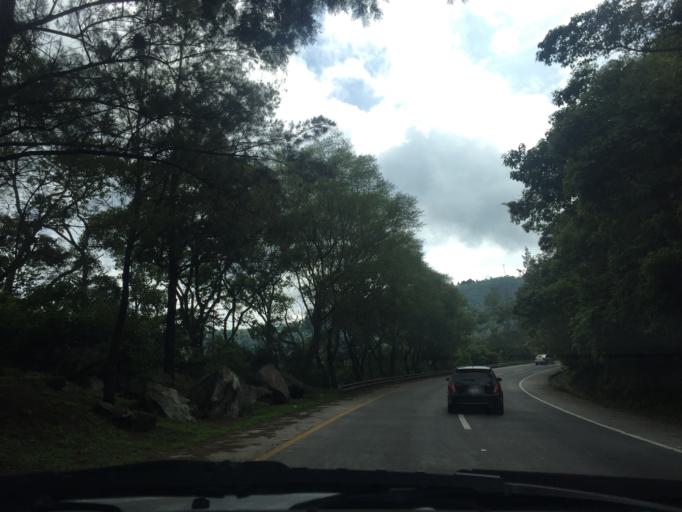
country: GT
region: Sacatepequez
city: Antigua Guatemala
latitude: 14.5593
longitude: -90.7093
